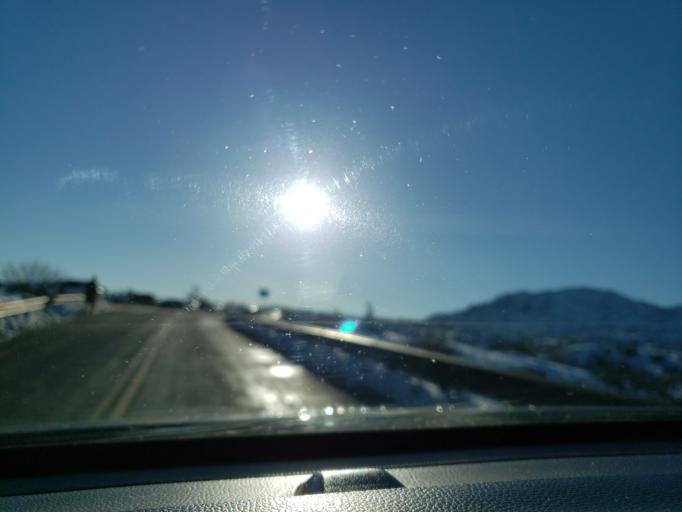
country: US
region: Arizona
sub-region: Maricopa County
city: Carefree
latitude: 33.8772
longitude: -111.8167
